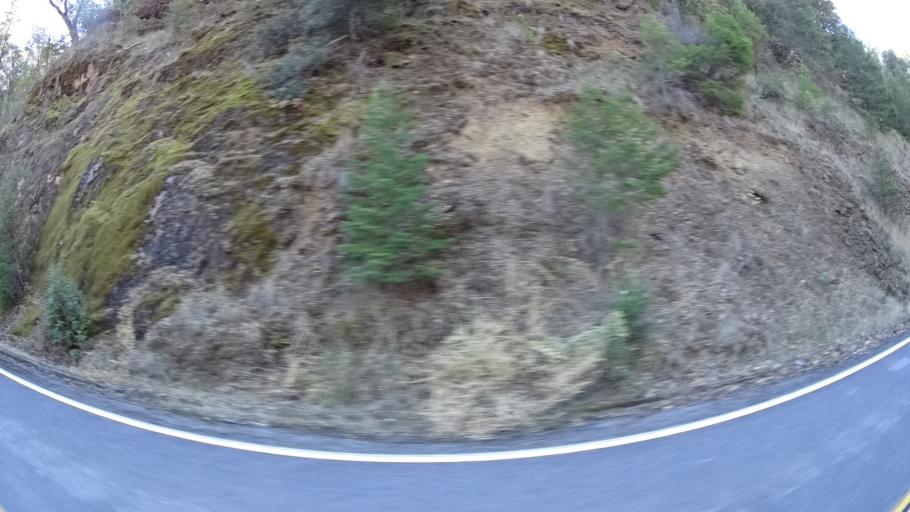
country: US
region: California
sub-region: Siskiyou County
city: Happy Camp
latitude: 41.3753
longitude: -123.4243
